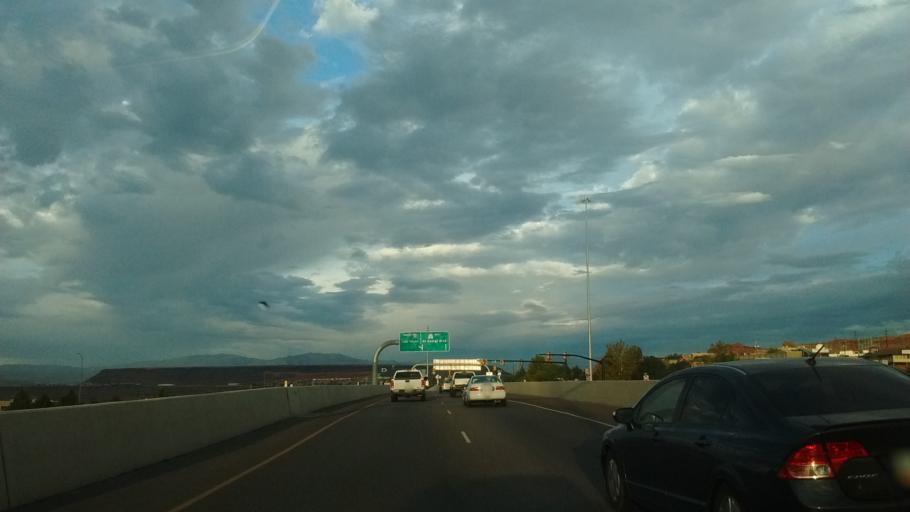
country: US
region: Utah
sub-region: Washington County
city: Saint George
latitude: 37.1097
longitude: -113.5573
